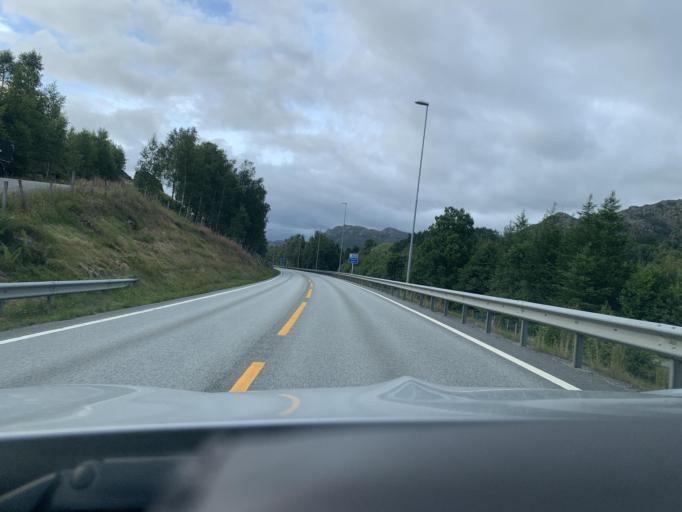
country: NO
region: Rogaland
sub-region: Bjerkreim
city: Vikesa
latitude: 58.6135
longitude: 6.0930
